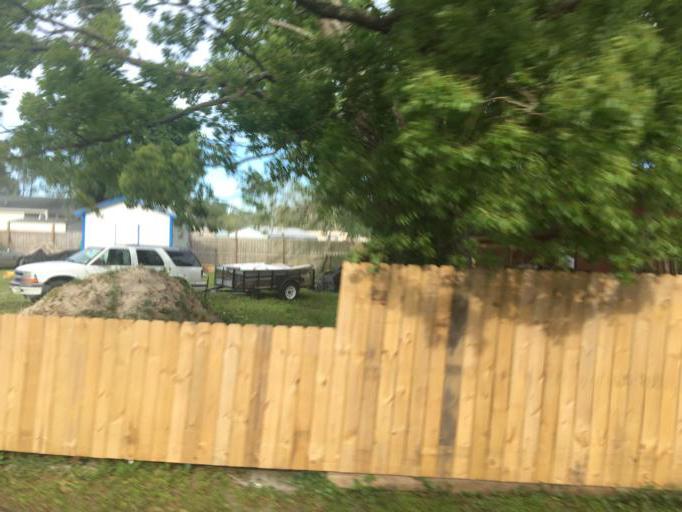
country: US
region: Florida
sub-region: Bay County
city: Panama City Beach
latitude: 30.1742
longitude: -85.7823
